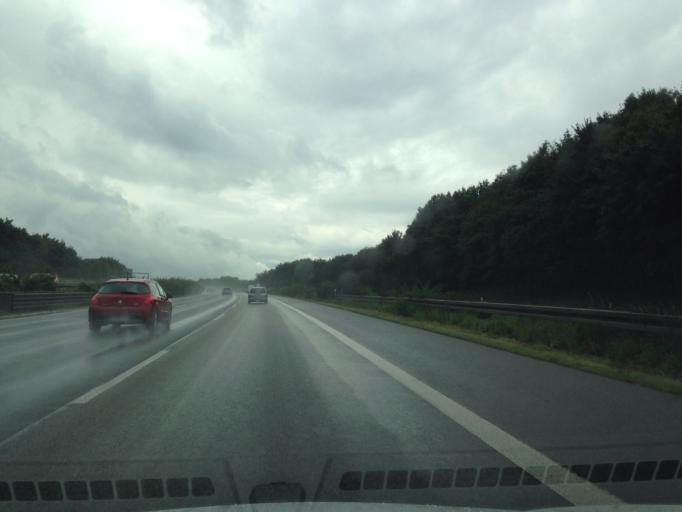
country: DE
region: North Rhine-Westphalia
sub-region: Regierungsbezirk Munster
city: Bottrop
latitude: 51.5559
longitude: 6.9287
